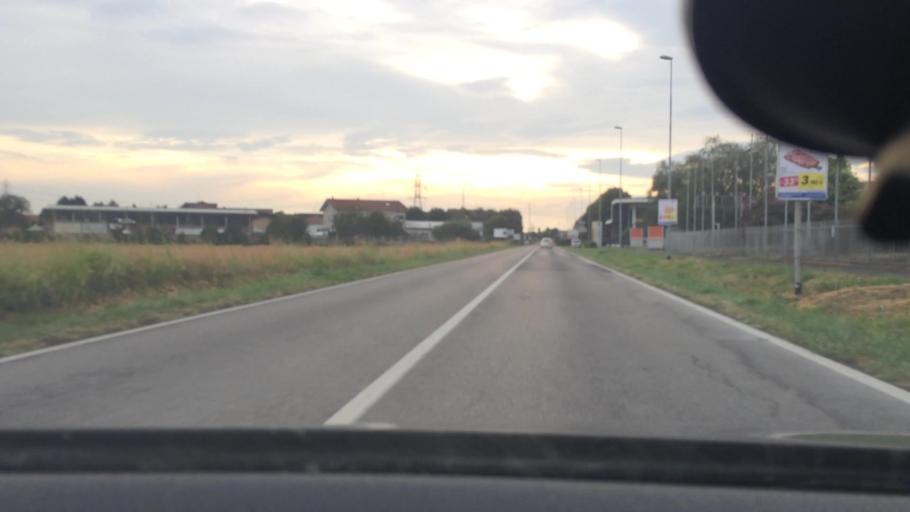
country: IT
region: Lombardy
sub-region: Provincia di Monza e Brianza
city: Nova Milanese
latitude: 45.5949
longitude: 9.1817
